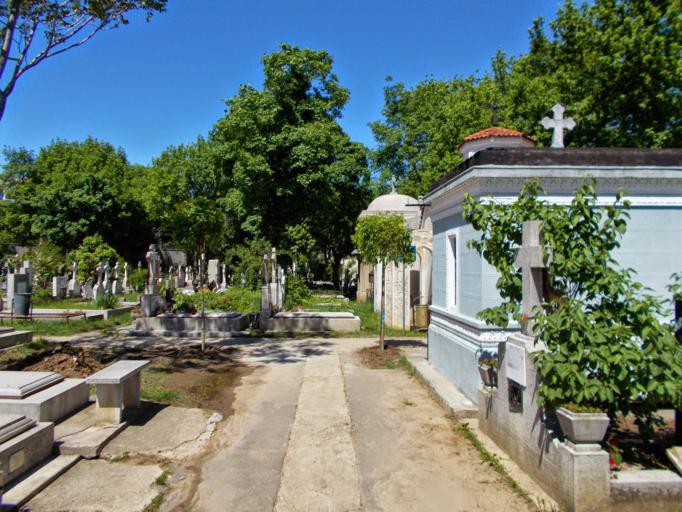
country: RO
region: Bucuresti
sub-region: Municipiul Bucuresti
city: Bucuresti
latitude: 44.4071
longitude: 26.0975
